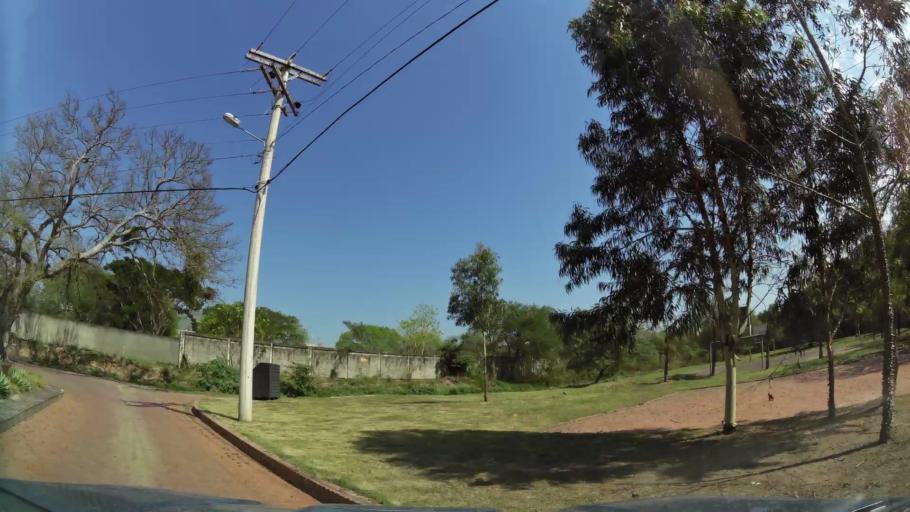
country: BO
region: Santa Cruz
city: Santa Cruz de la Sierra
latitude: -17.7518
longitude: -63.1977
